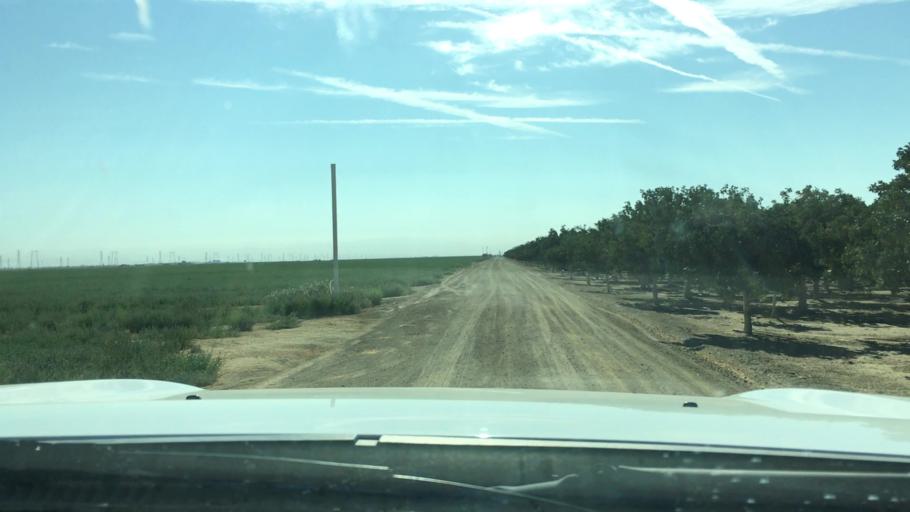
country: US
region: California
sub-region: Kern County
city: Buttonwillow
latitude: 35.3766
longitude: -119.3946
